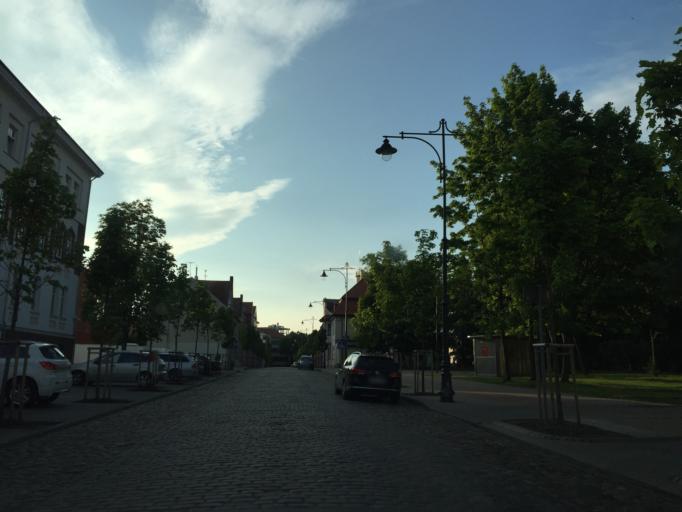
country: LT
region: Klaipedos apskritis
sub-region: Klaipeda
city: Klaipeda
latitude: 55.7149
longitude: 21.1362
